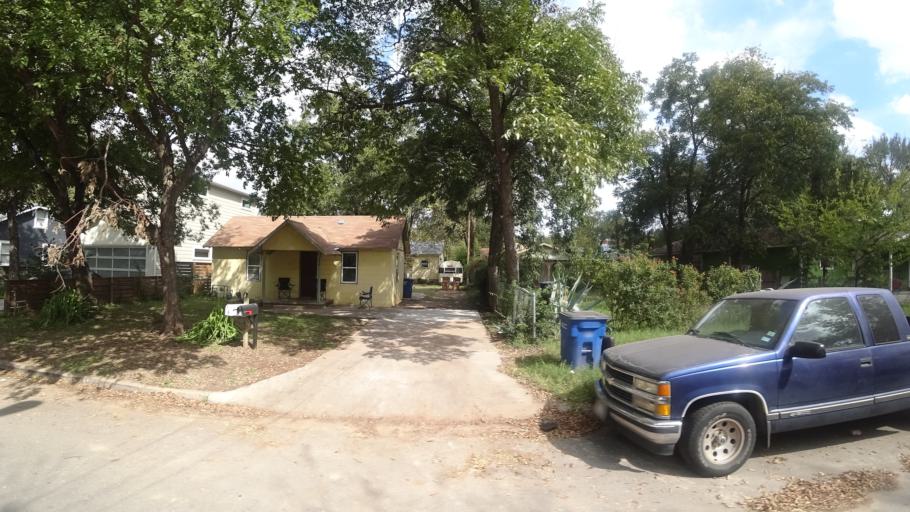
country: US
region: Texas
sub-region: Travis County
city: Austin
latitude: 30.2551
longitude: -97.7129
